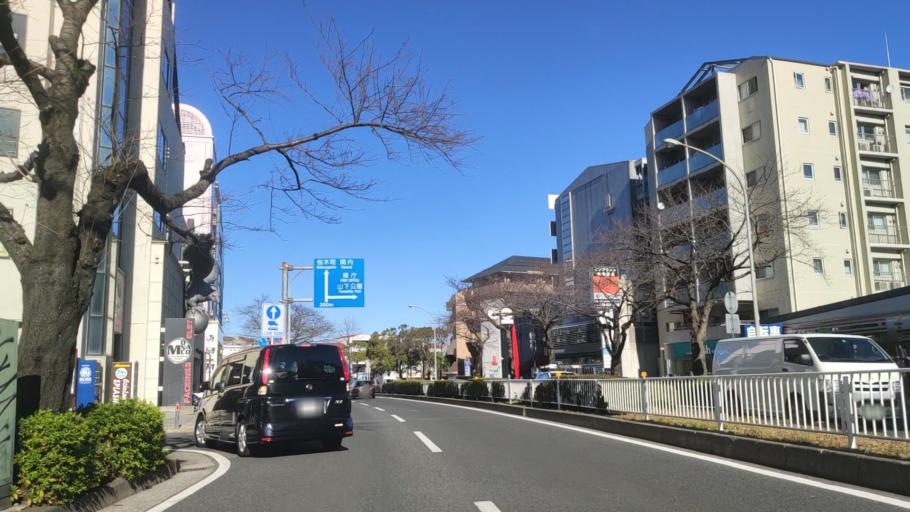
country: JP
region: Kanagawa
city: Yokohama
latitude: 35.4268
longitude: 139.6666
